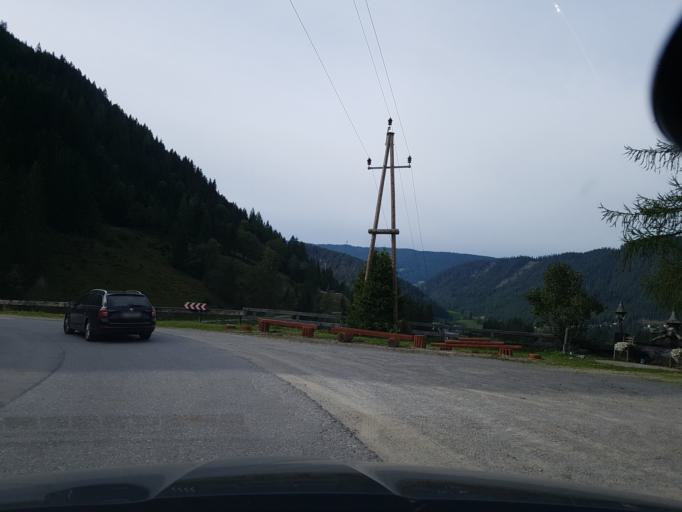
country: AT
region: Salzburg
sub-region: Politischer Bezirk Sankt Johann im Pongau
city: Forstau
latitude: 47.3656
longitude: 13.5564
